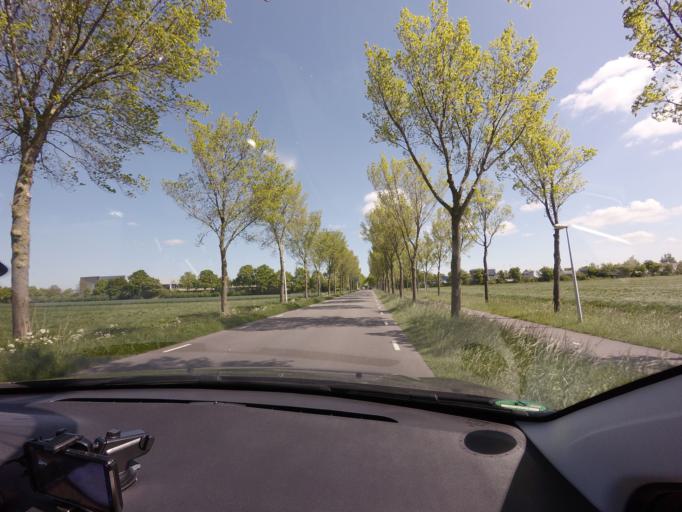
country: NL
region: North Holland
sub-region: Gemeente Beemster
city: Halfweg
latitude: 52.5516
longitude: 4.8980
